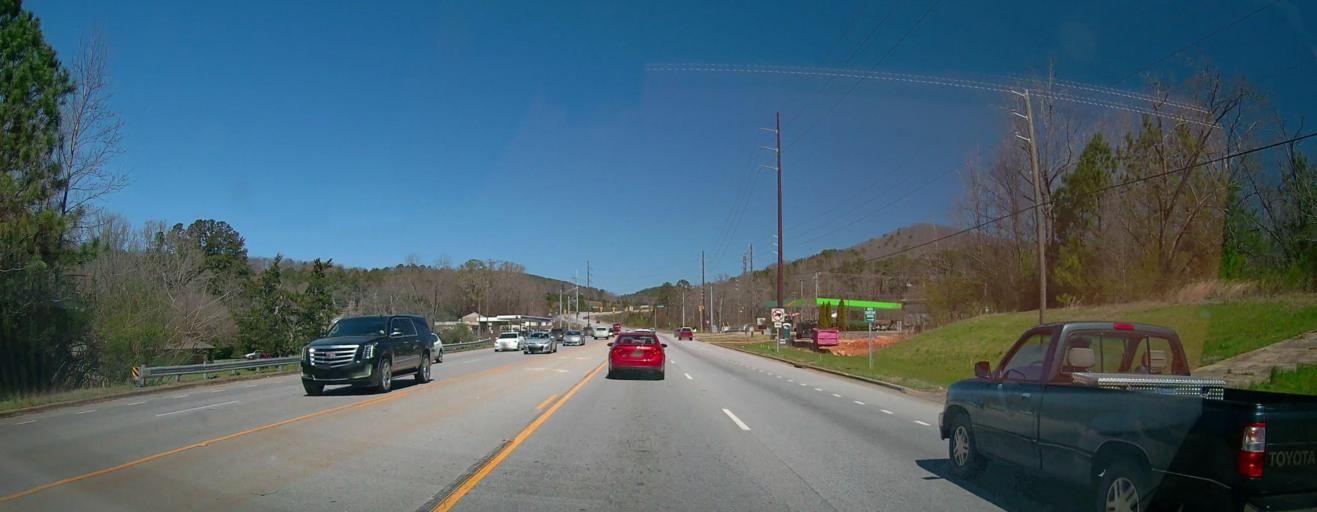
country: US
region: Alabama
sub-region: Calhoun County
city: Anniston
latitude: 33.6420
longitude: -85.7859
